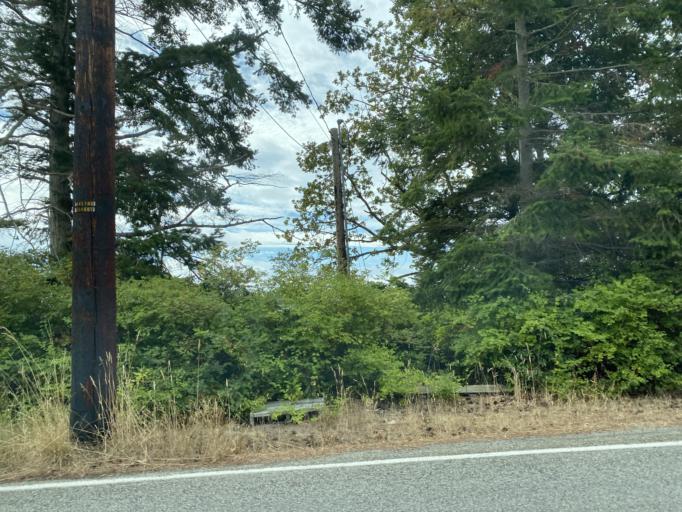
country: US
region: Washington
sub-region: Island County
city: Coupeville
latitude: 48.2393
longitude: -122.6934
